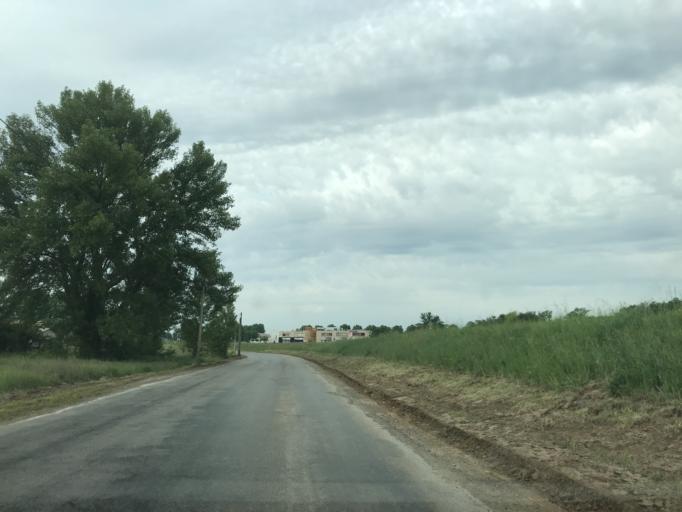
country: FR
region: Provence-Alpes-Cote d'Azur
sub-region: Departement des Alpes-de-Haute-Provence
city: Manosque
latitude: 43.8220
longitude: 5.8017
